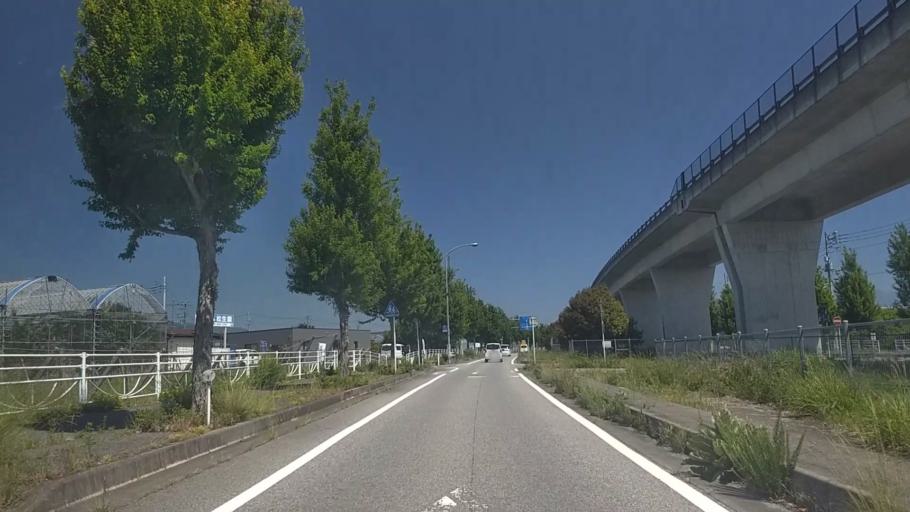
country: JP
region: Yamanashi
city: Ryuo
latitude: 35.6337
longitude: 138.4720
